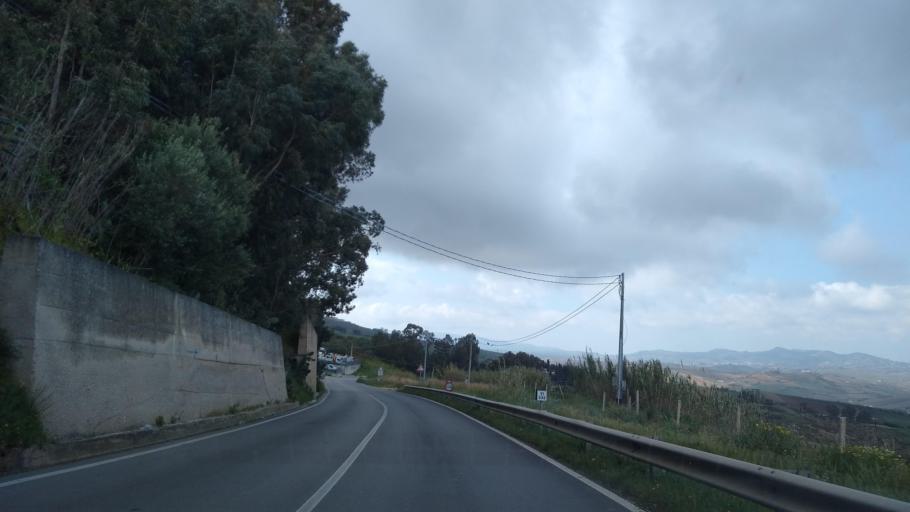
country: IT
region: Sicily
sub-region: Trapani
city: Alcamo
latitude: 37.9766
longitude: 12.9355
